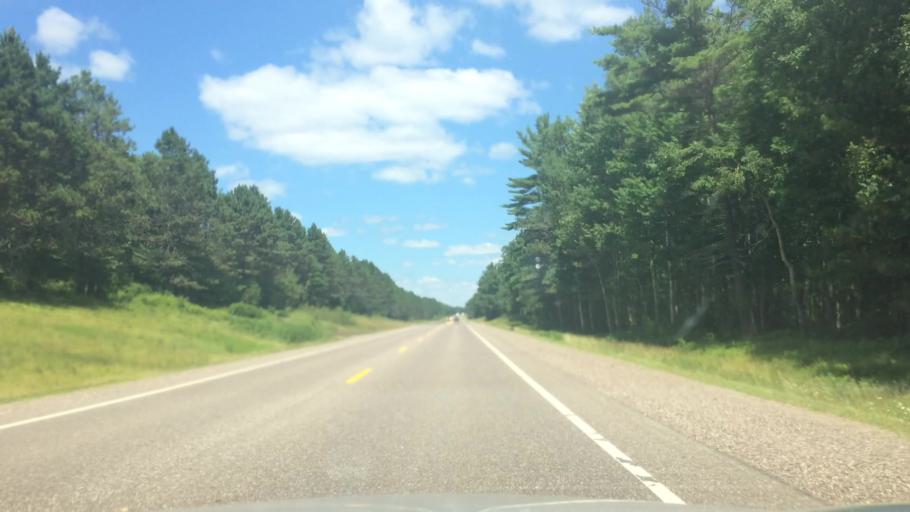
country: US
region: Wisconsin
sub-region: Vilas County
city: Lac du Flambeau
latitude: 45.9600
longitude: -89.7003
